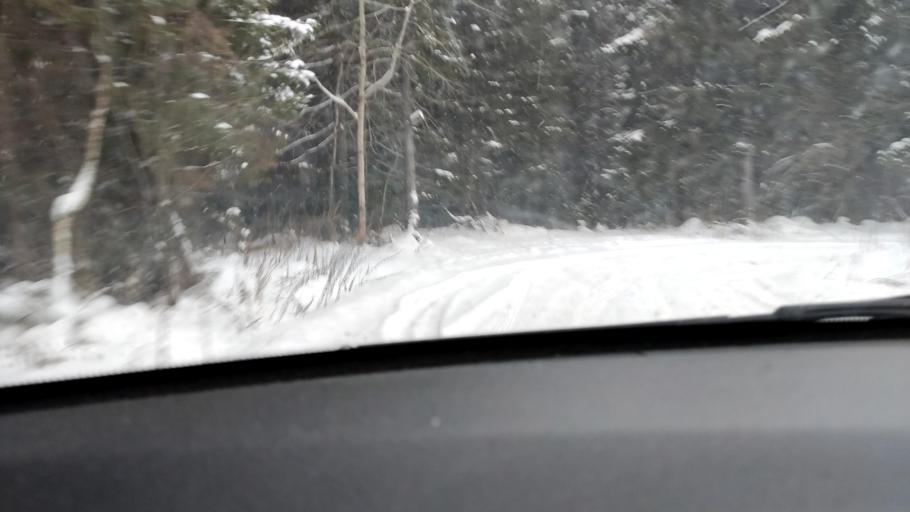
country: RU
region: Perm
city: Krasnokamsk
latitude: 57.9997
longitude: 55.7731
